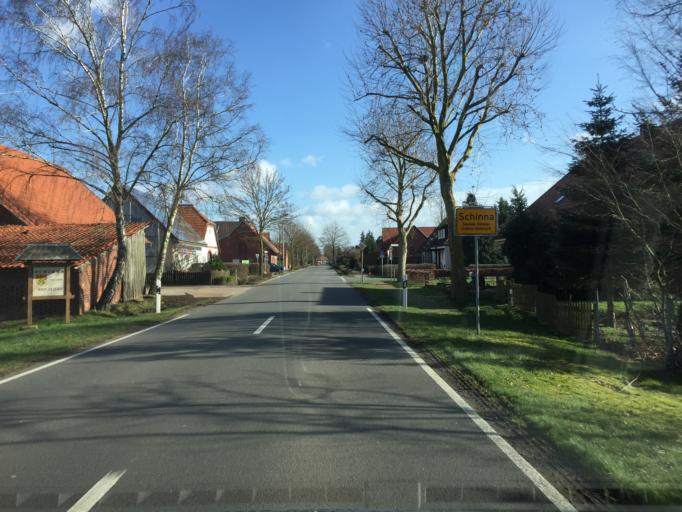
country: DE
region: Lower Saxony
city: Stolzenau
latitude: 52.5372
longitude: 9.0651
